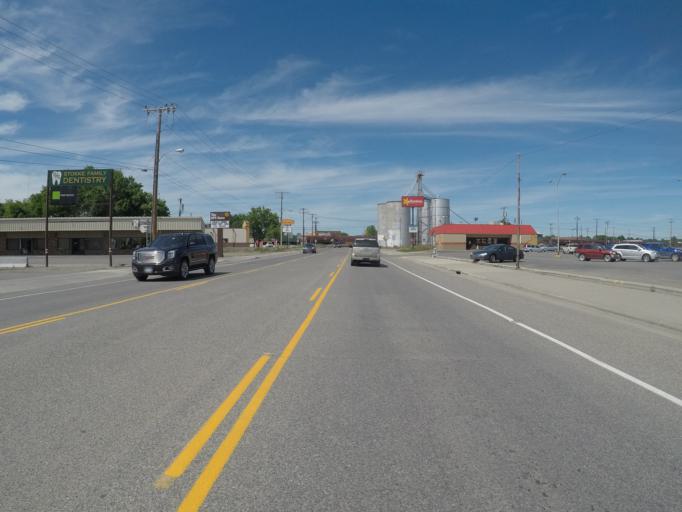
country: US
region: Montana
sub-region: Yellowstone County
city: Laurel
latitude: 45.6666
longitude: -108.7715
